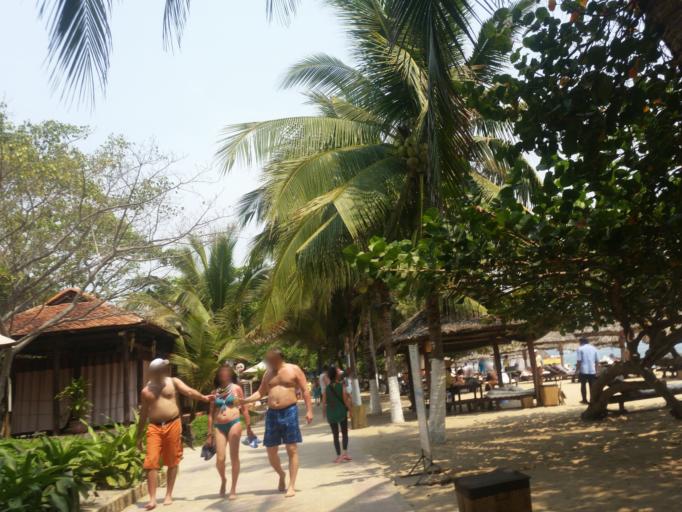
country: VN
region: Khanh Hoa
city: Nha Trang
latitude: 12.2288
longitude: 109.2000
